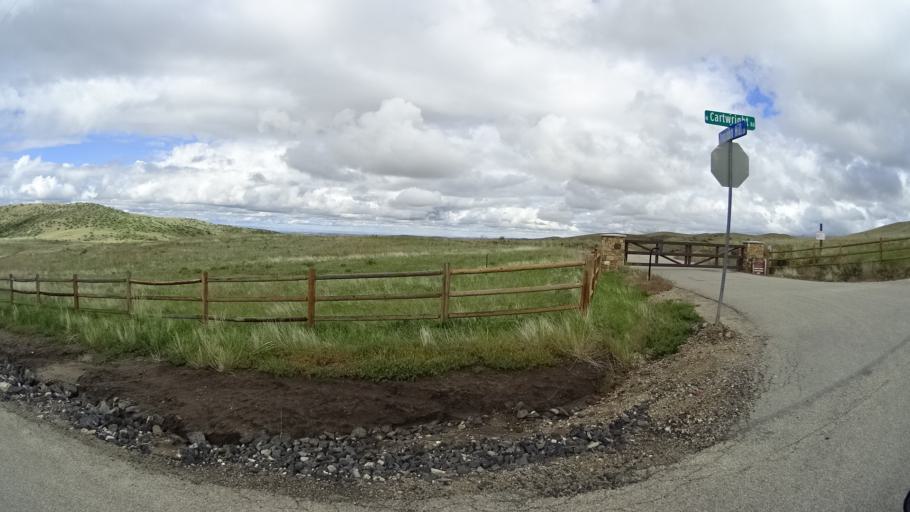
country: US
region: Idaho
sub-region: Ada County
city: Garden City
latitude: 43.7404
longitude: -116.2259
